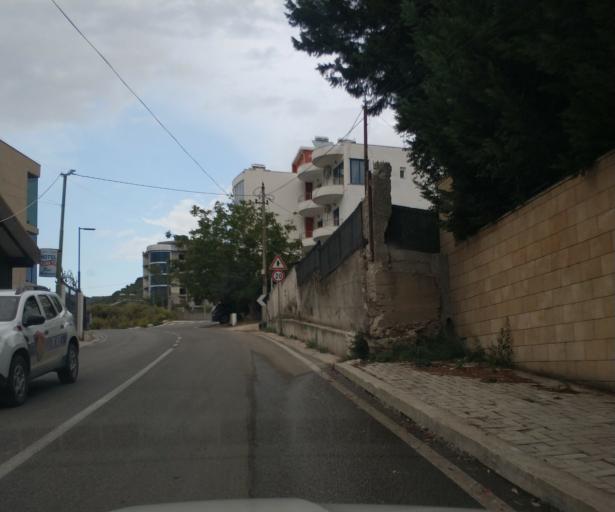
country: AL
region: Vlore
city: Vlore
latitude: 40.4343
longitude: 19.4959
